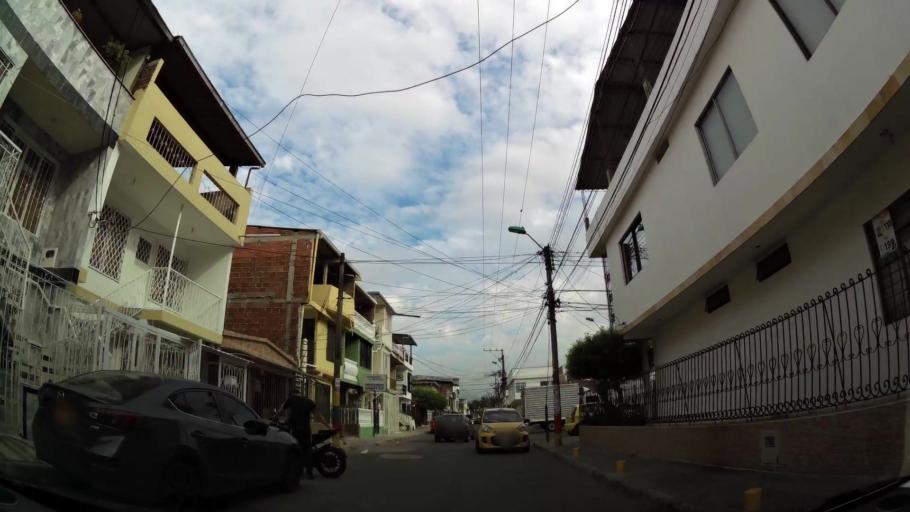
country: CO
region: Valle del Cauca
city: Cali
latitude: 3.4725
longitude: -76.4911
